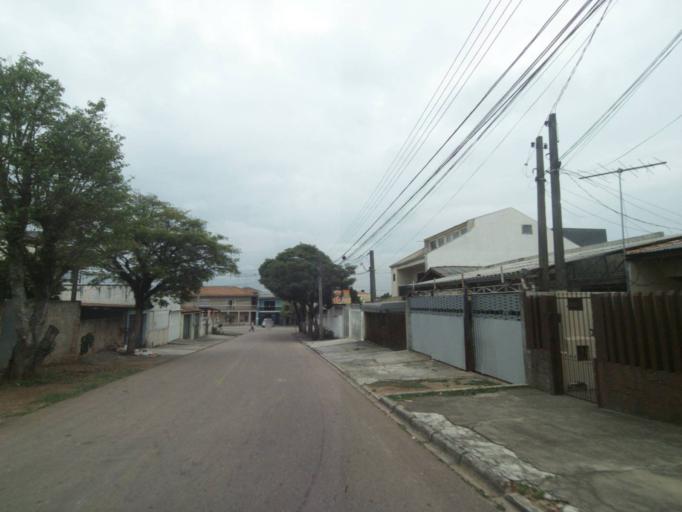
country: BR
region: Parana
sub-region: Sao Jose Dos Pinhais
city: Sao Jose dos Pinhais
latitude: -25.5498
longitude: -49.2707
